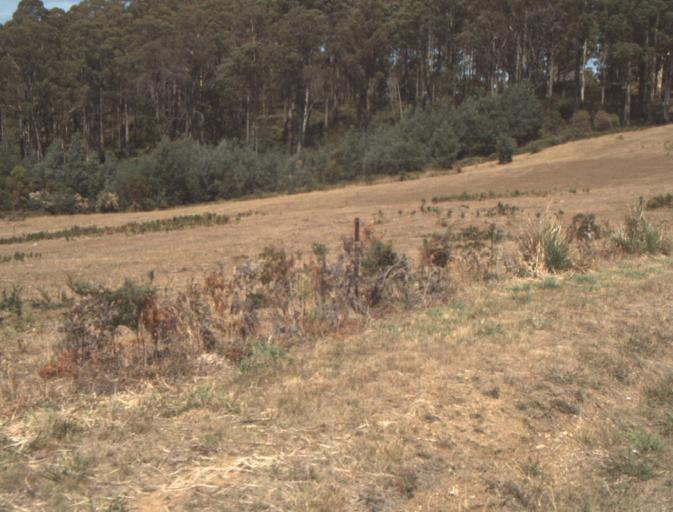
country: AU
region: Tasmania
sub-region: Launceston
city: Mayfield
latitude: -41.2732
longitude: 147.1275
